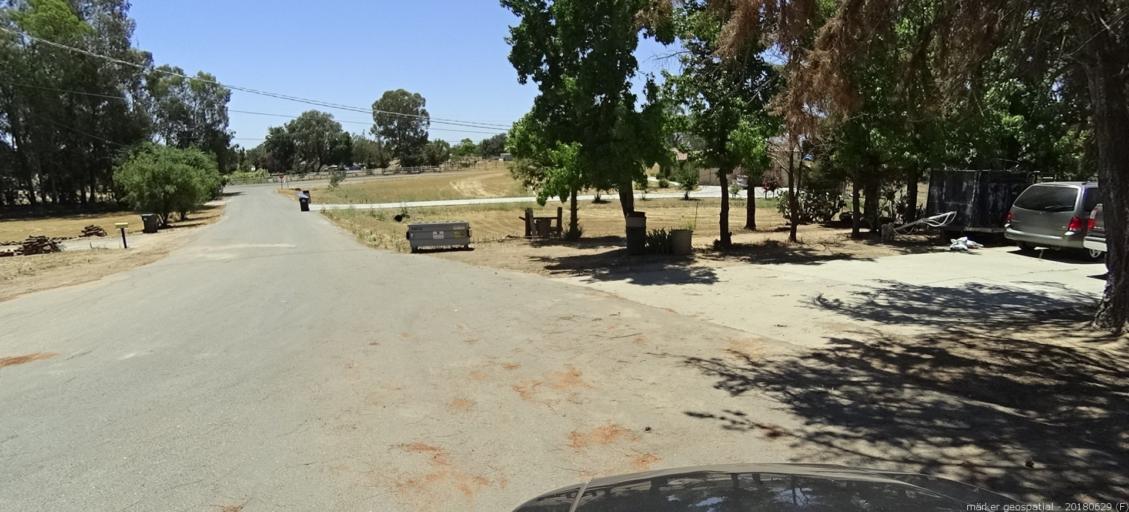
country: US
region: California
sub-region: Madera County
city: Parksdale
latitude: 36.9973
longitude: -119.9880
